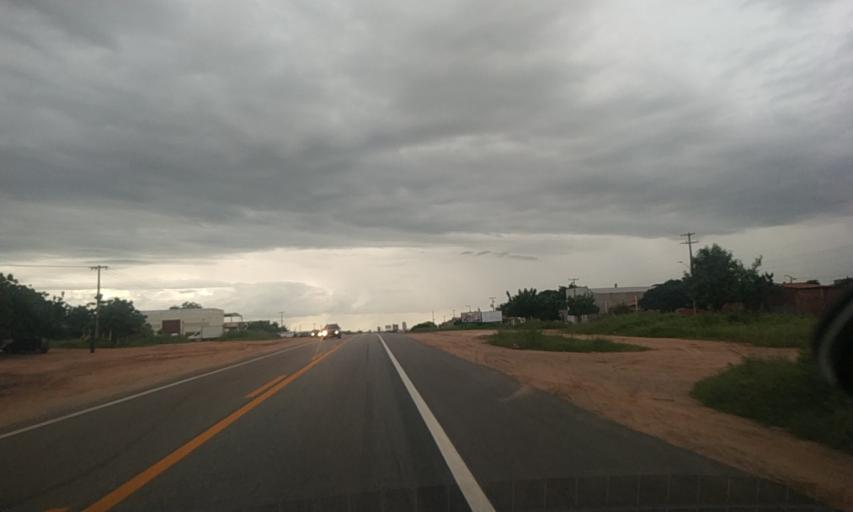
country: BR
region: Rio Grande do Norte
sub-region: Mossoro
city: Mossoro
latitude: -5.1885
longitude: -37.3058
